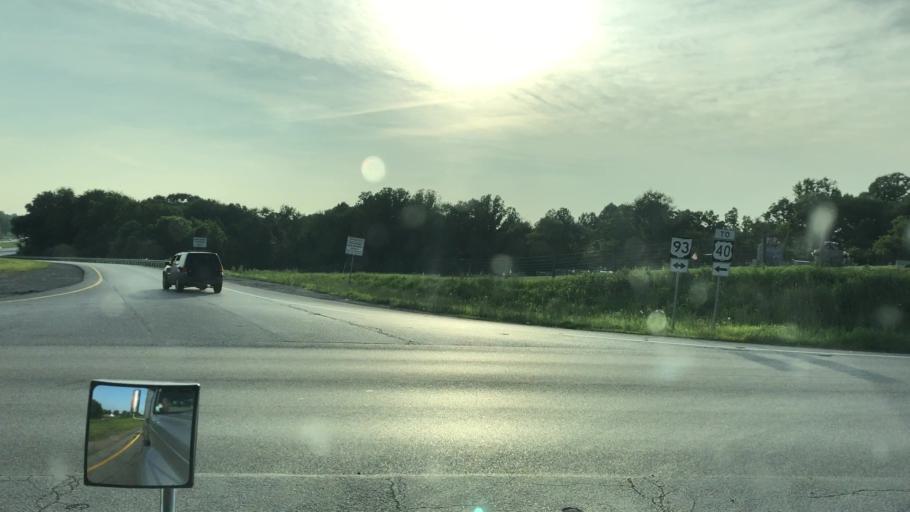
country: US
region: Ohio
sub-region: Muskingum County
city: Pleasant Grove
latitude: 39.9506
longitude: -81.9601
